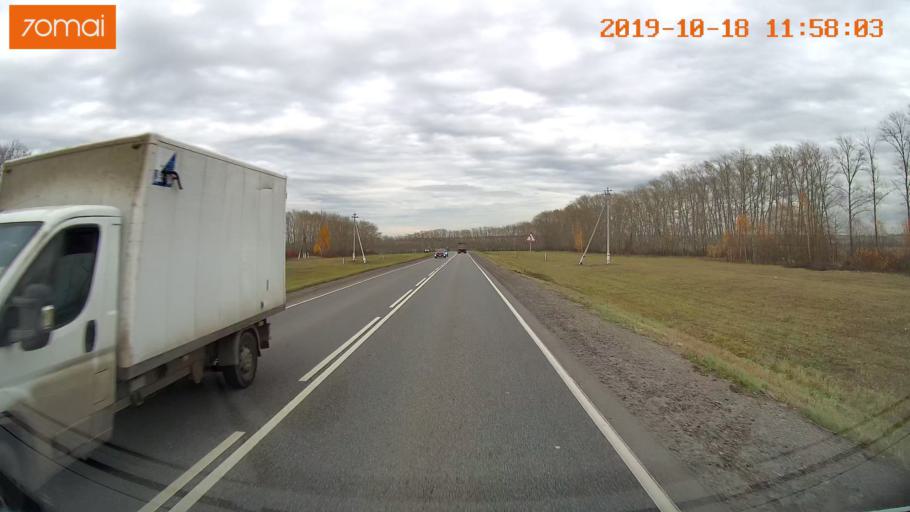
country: RU
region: Rjazan
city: Mikhaylov
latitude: 54.2685
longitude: 39.1594
